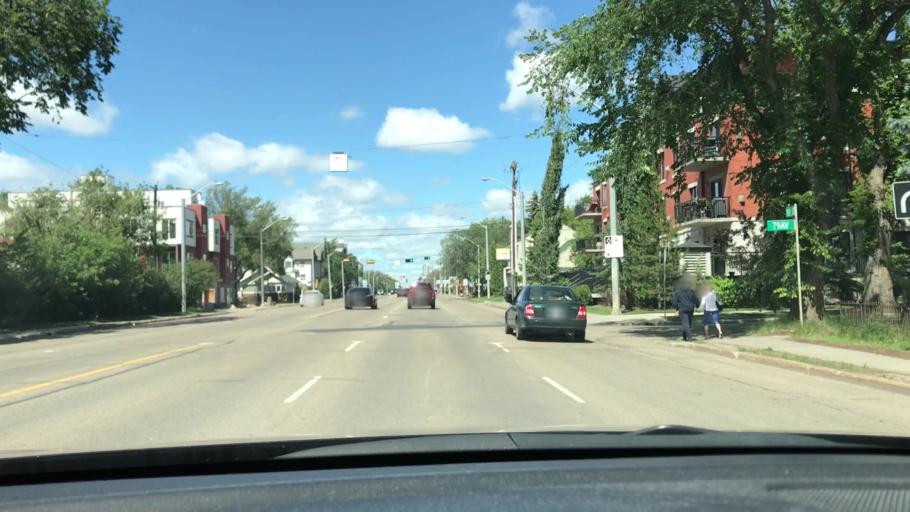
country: CA
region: Alberta
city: Edmonton
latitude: 53.5149
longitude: -113.5120
